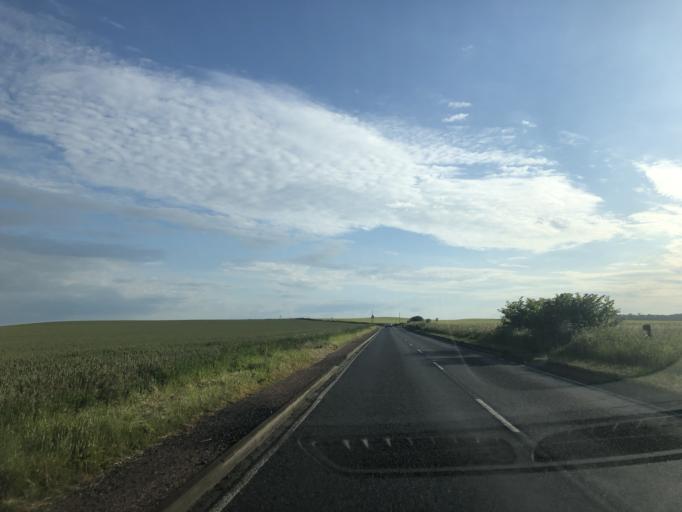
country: GB
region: Scotland
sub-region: Fife
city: Saint Monance
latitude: 56.2031
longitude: -2.7857
